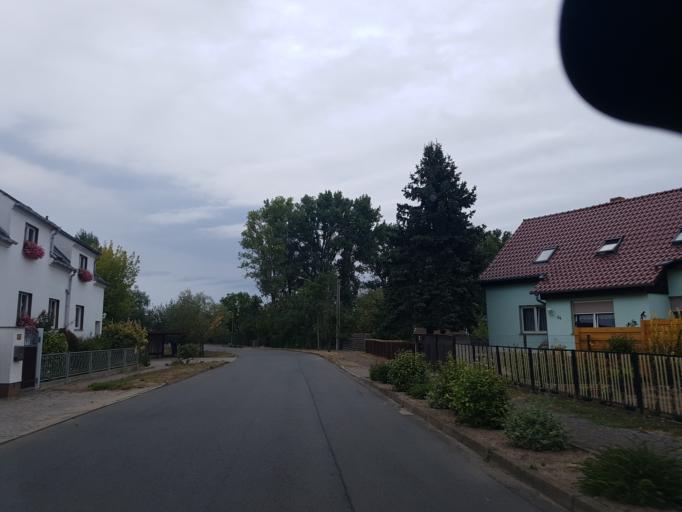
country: DE
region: Saxony-Anhalt
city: Prettin
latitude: 51.7027
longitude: 12.9003
